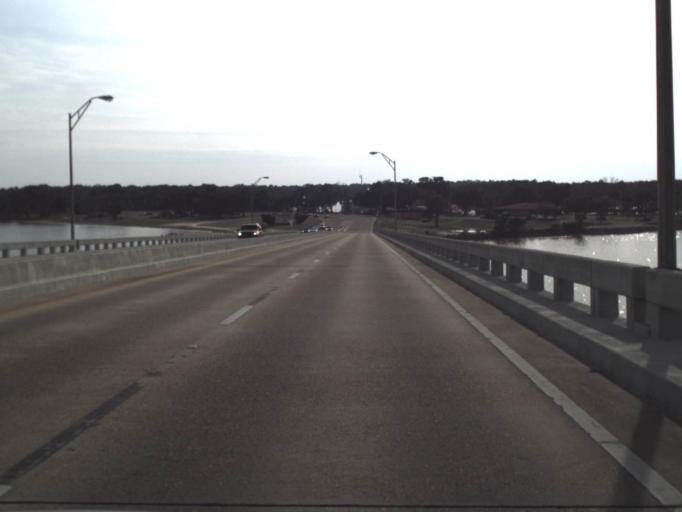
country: US
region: Florida
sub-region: Bay County
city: Tyndall Air Force Base
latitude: 30.1034
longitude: -85.6094
